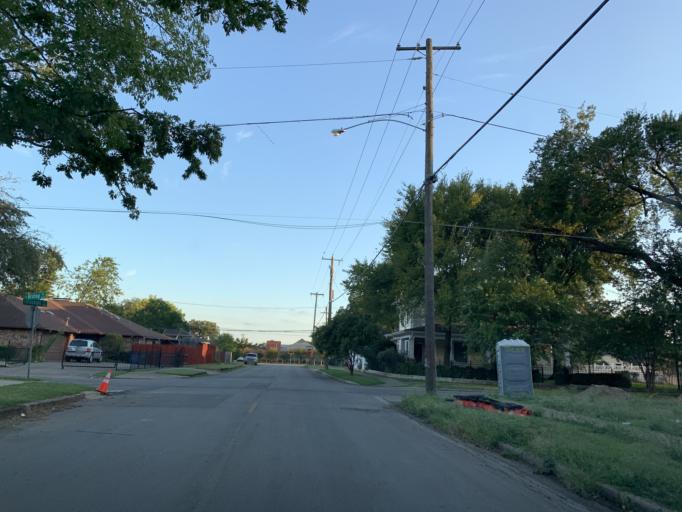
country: US
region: Texas
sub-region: Dallas County
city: Dallas
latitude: 32.7395
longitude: -96.8283
